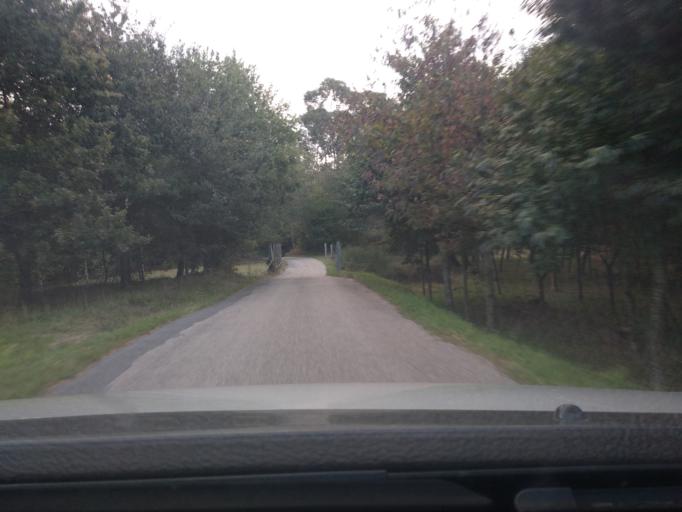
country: ES
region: Galicia
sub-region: Provincia de Pontevedra
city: Moana
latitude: 42.3053
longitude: -8.6969
